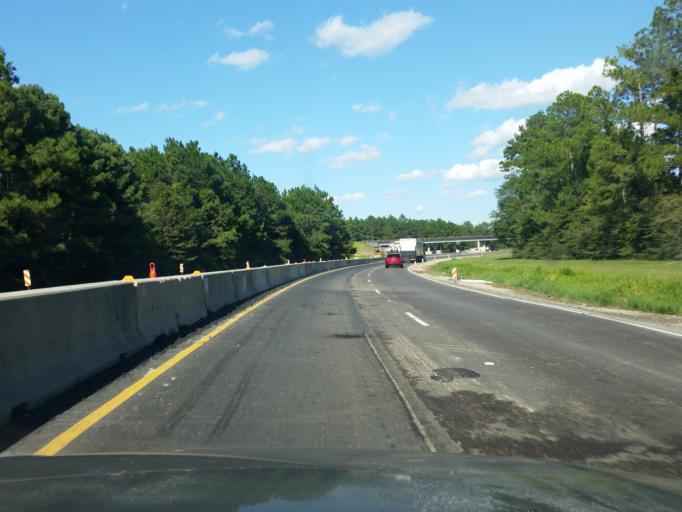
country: US
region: Louisiana
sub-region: Saint Tammany Parish
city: Slidell
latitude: 30.3032
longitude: -89.7404
